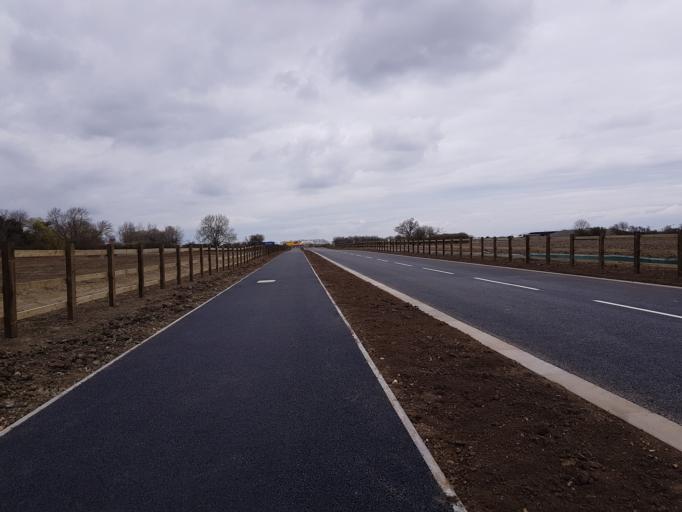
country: GB
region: England
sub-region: Cambridgeshire
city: Girton
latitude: 52.2410
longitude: 0.0481
